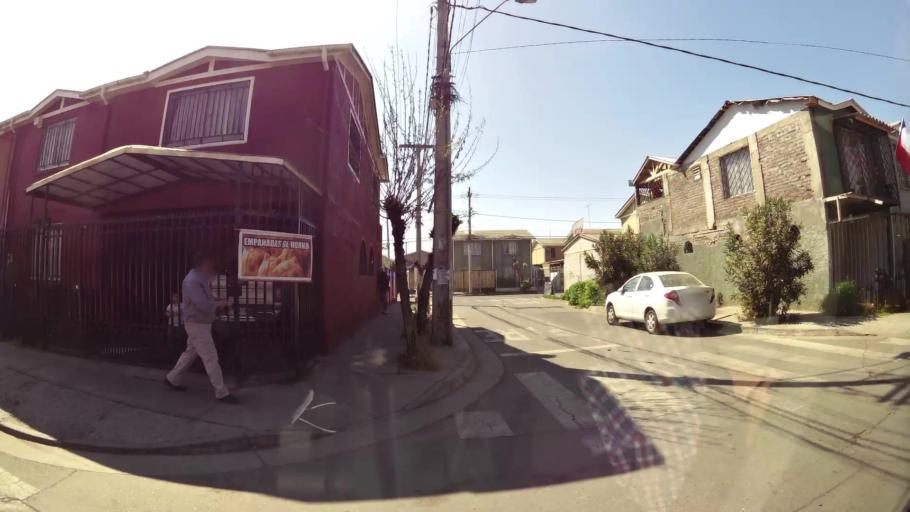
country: CL
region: Santiago Metropolitan
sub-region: Provincia de Santiago
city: Lo Prado
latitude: -33.3502
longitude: -70.7364
